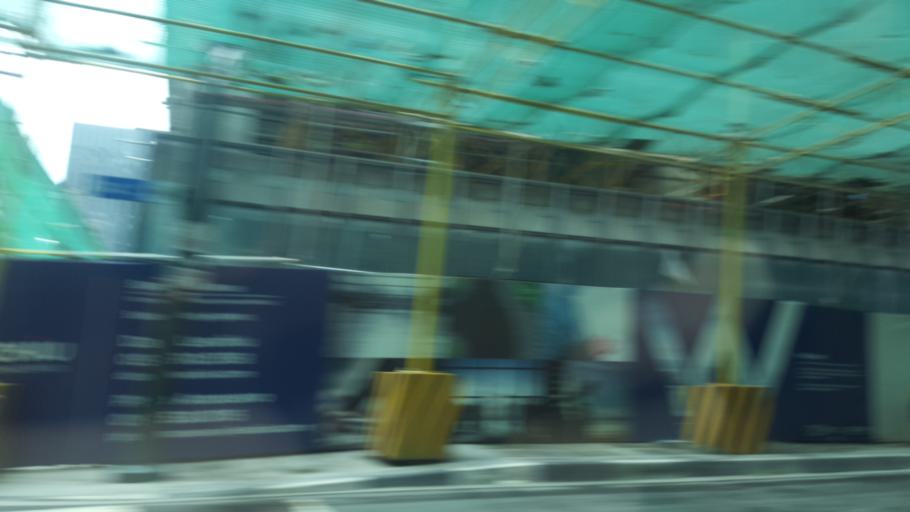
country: PH
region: Metro Manila
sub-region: Makati City
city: Makati City
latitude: 14.5543
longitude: 121.0540
